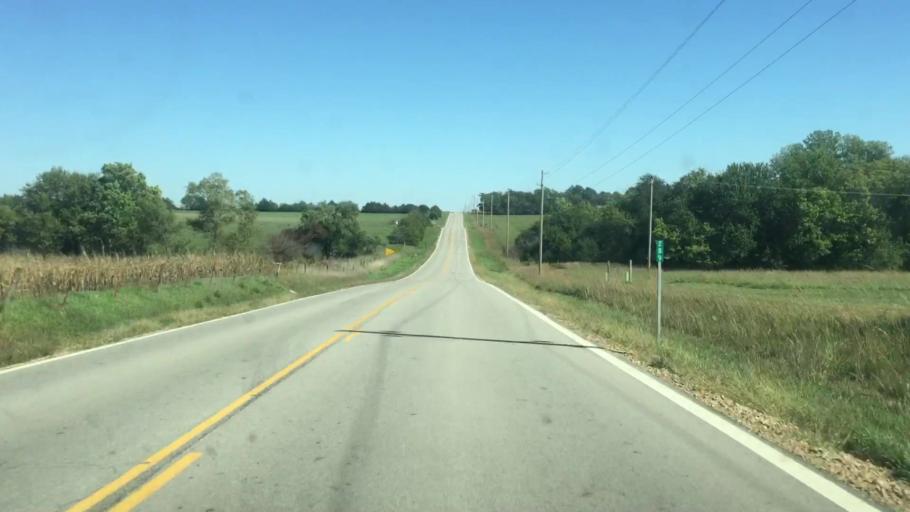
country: US
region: Kansas
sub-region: Jackson County
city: Holton
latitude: 39.5949
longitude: -95.7060
